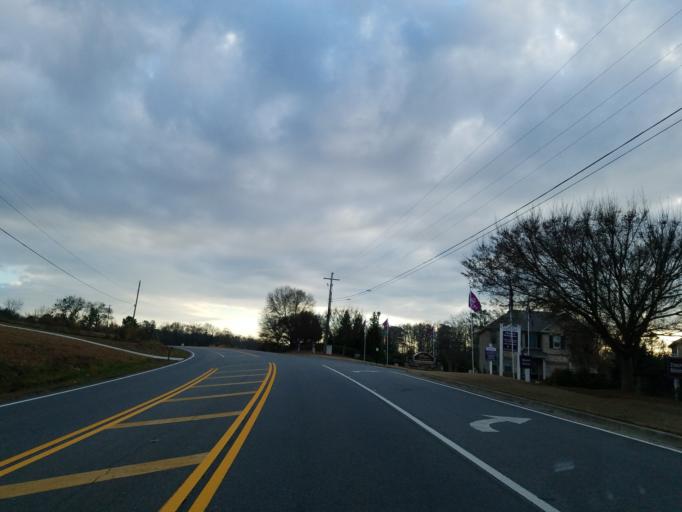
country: US
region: Georgia
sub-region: Forsyth County
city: Cumming
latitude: 34.2926
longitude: -84.0880
